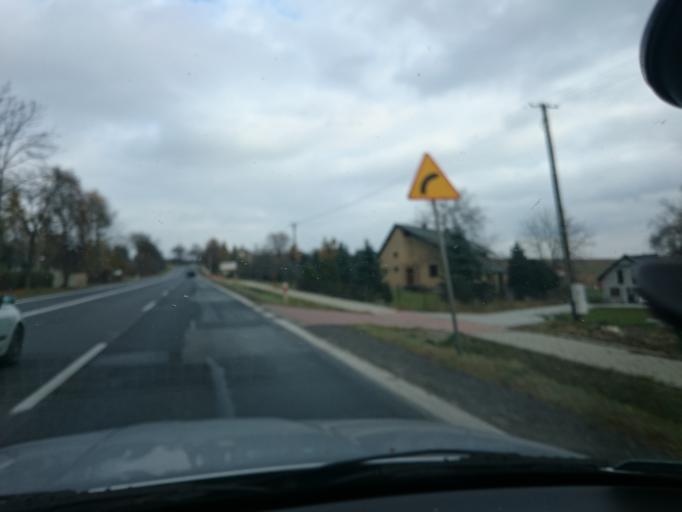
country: PL
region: Lesser Poland Voivodeship
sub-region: Powiat krakowski
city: Michalowice
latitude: 50.1771
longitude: 19.9889
